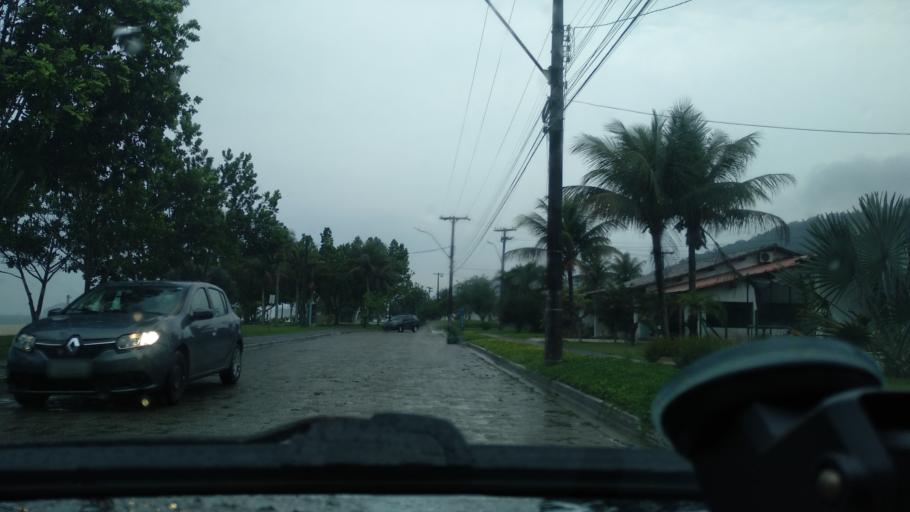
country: BR
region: Rio de Janeiro
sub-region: Angra Dos Reis
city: Angra dos Reis
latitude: -23.0289
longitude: -44.5368
